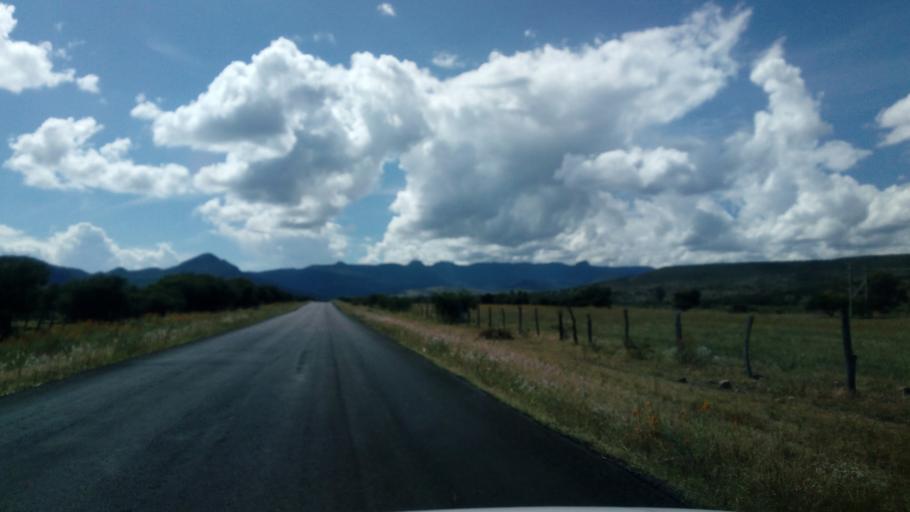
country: MX
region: Durango
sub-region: Durango
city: Jose Refugio Salcido
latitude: 23.8085
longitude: -104.4839
